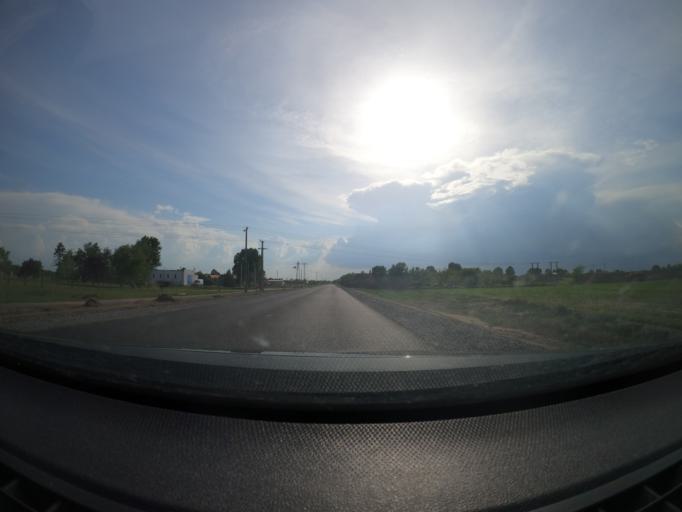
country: HU
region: Hajdu-Bihar
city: Vamospercs
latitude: 47.5264
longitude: 21.9197
